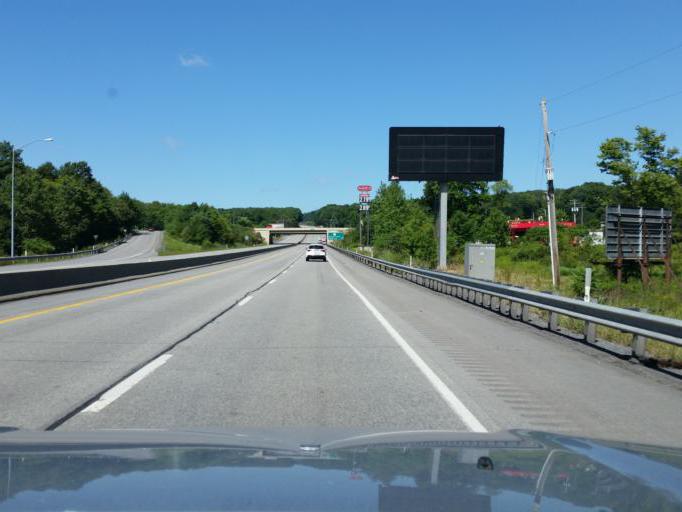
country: US
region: Pennsylvania
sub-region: Cambria County
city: Mundys Corner
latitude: 40.4497
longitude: -78.8353
